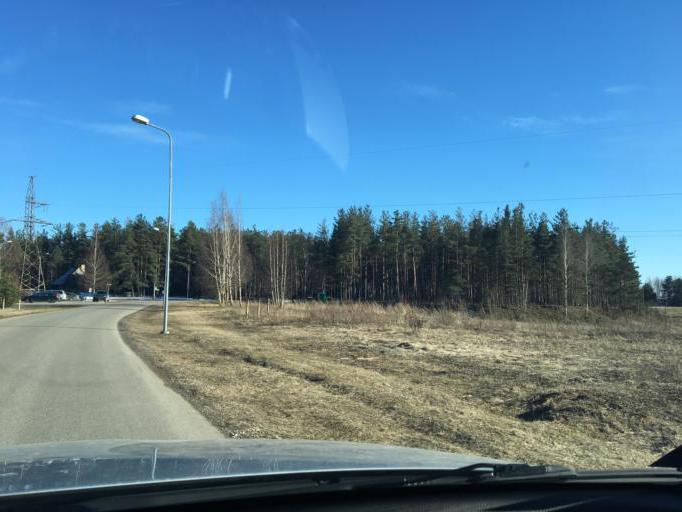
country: LV
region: Jekabpils Rajons
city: Jekabpils
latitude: 56.4852
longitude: 25.8509
